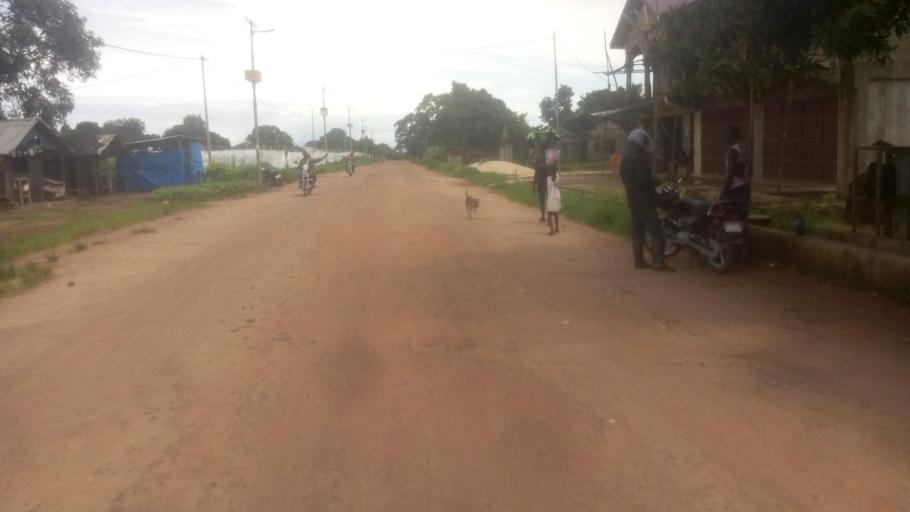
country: SL
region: Northern Province
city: Masoyila
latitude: 8.6020
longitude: -13.1966
